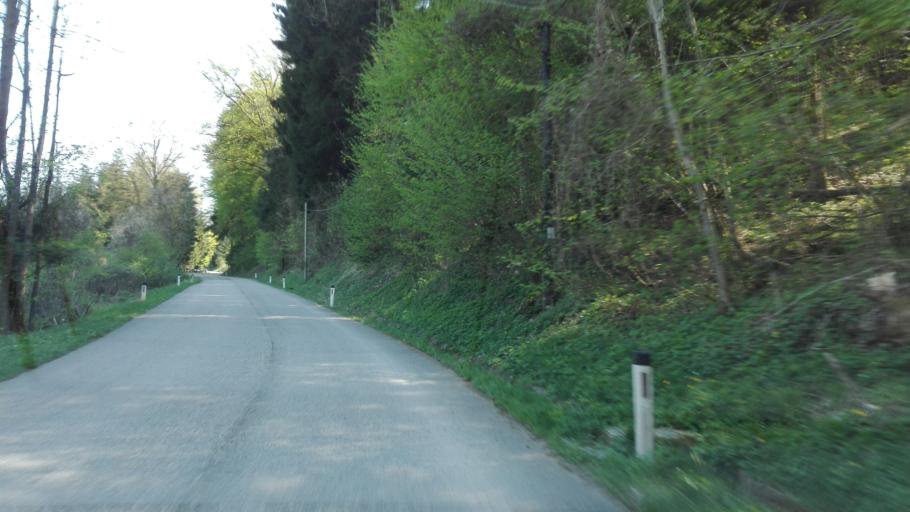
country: AT
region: Upper Austria
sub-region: Politischer Bezirk Rohrbach
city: Atzesberg
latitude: 48.4346
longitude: 13.9154
